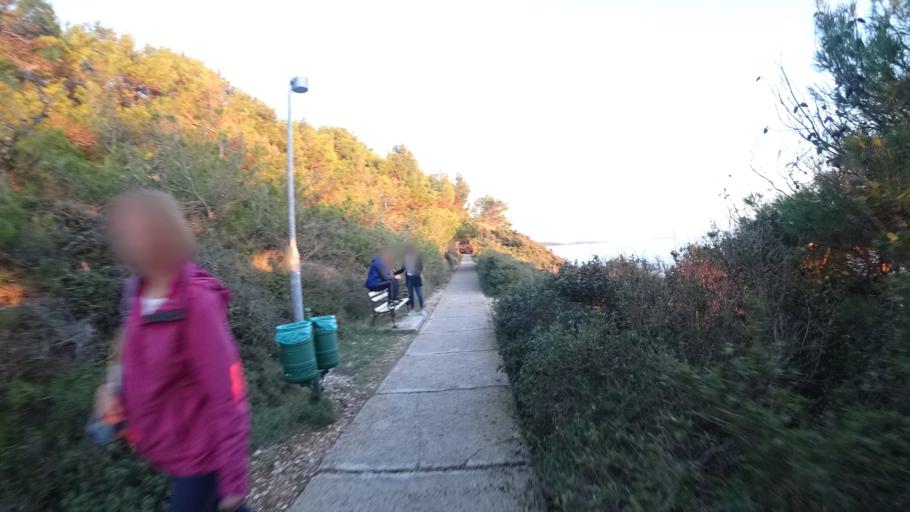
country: HR
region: Primorsko-Goranska
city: Mali Losinj
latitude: 44.5243
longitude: 14.4500
